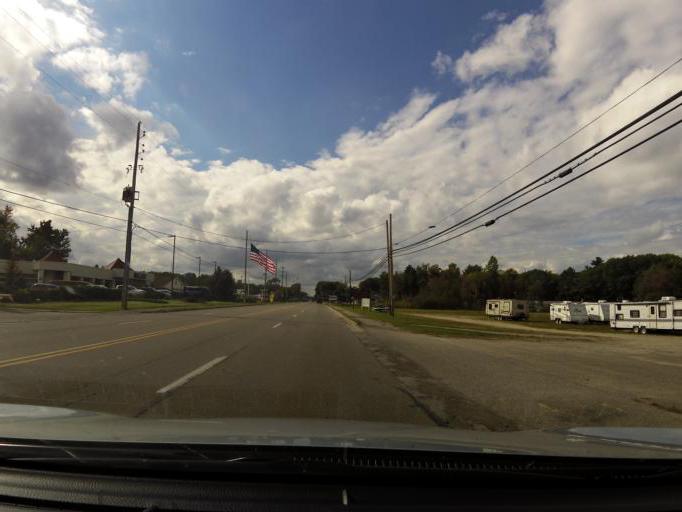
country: US
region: Michigan
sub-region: Roscommon County
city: Prudenville
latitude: 44.2987
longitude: -84.6892
